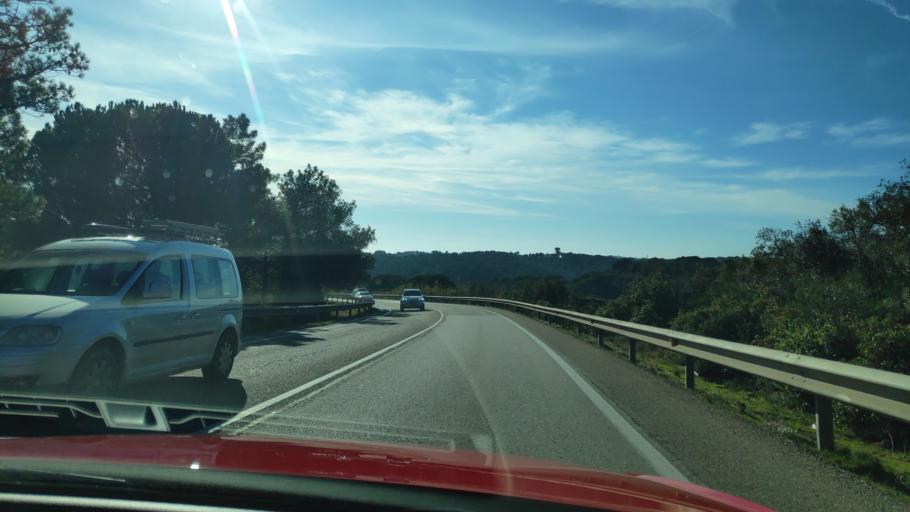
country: ES
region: Catalonia
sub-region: Provincia de Girona
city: Lloret de Mar
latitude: 41.7218
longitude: 2.8251
